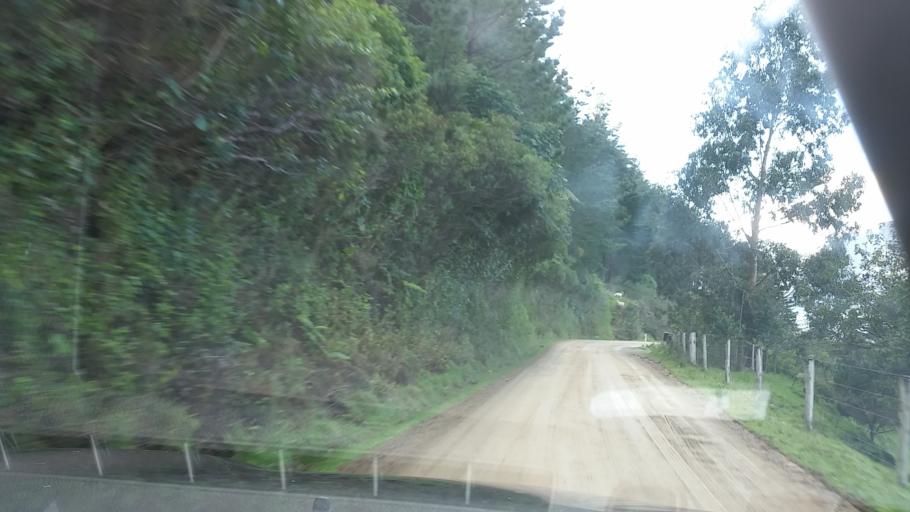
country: NZ
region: Marlborough
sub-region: Marlborough District
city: Picton
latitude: -40.9852
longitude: 173.8271
